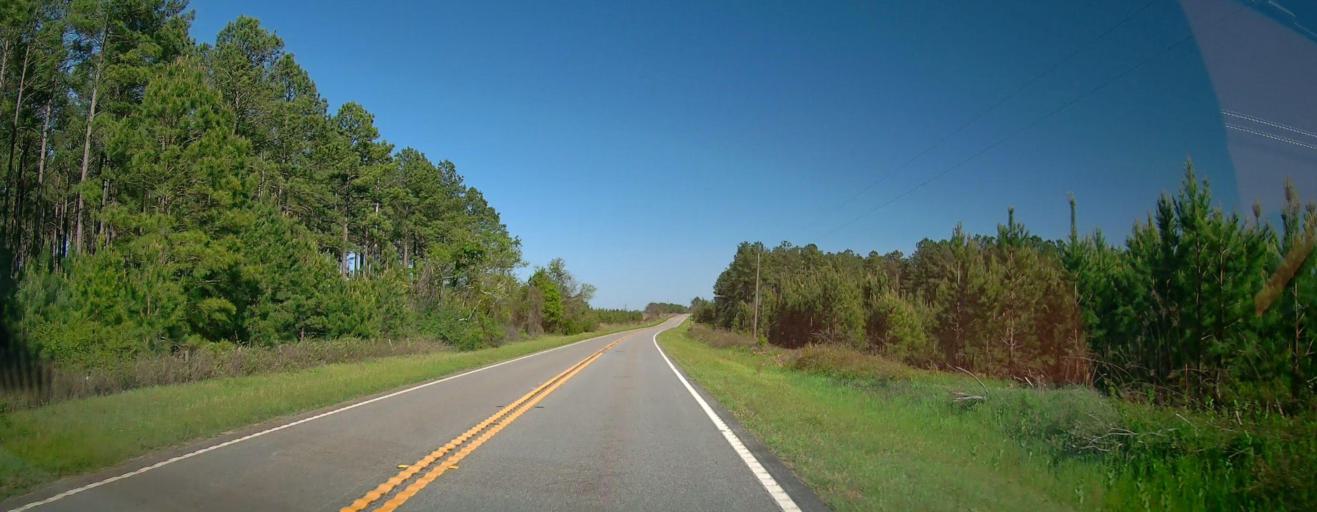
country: US
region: Georgia
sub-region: Dooly County
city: Unadilla
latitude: 32.2551
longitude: -83.6379
